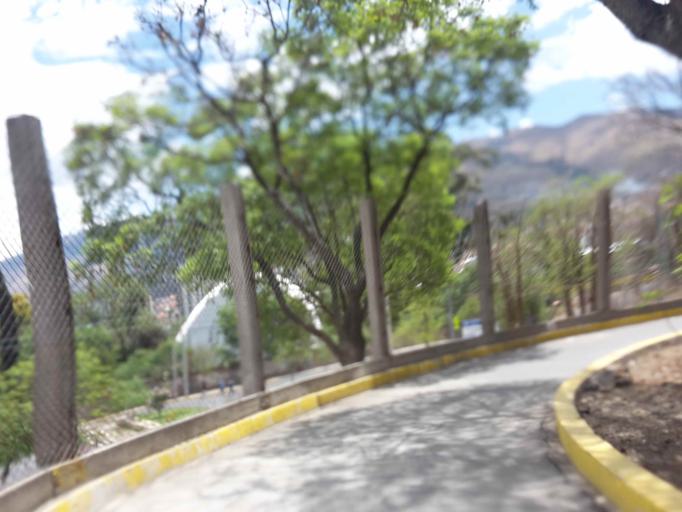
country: BO
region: Cochabamba
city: Cochabamba
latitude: -17.3784
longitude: -66.1390
